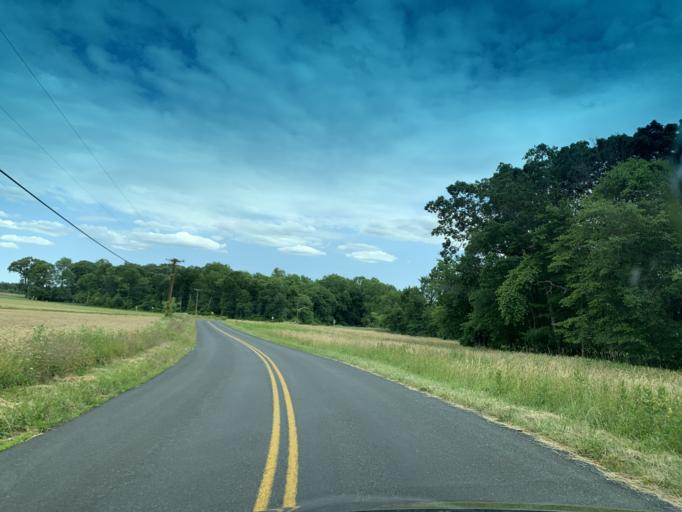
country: US
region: Maryland
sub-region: Harford County
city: Jarrettsville
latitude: 39.6152
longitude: -76.4989
